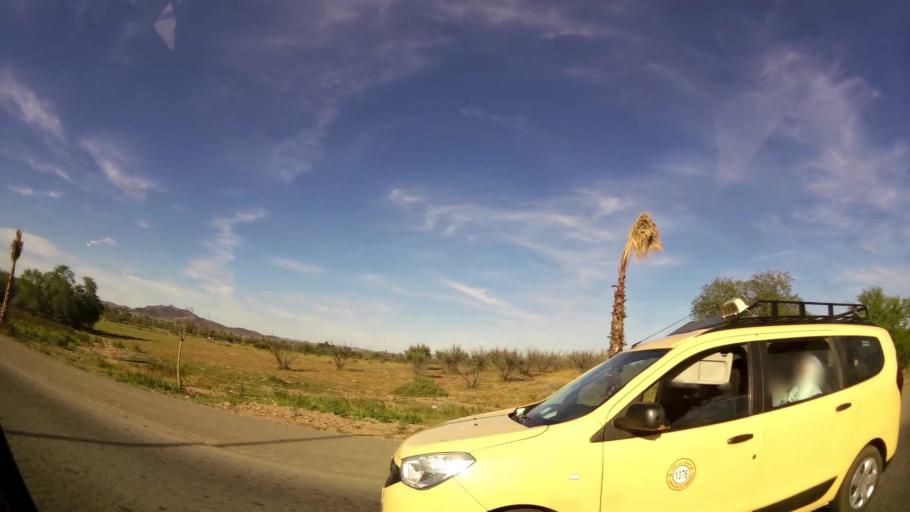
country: MA
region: Marrakech-Tensift-Al Haouz
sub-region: Marrakech
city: Marrakesh
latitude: 31.6892
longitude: -8.0541
